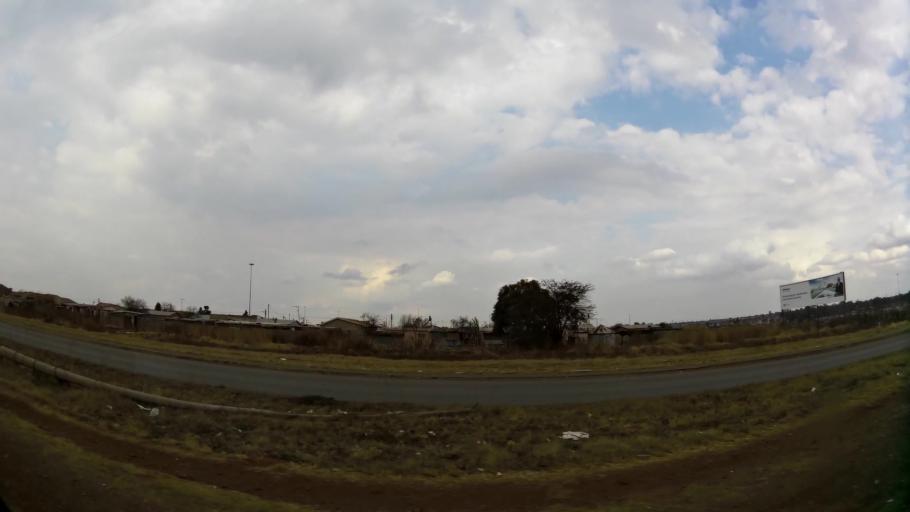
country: ZA
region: Gauteng
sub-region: Sedibeng District Municipality
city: Vanderbijlpark
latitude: -26.6615
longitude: 27.8442
